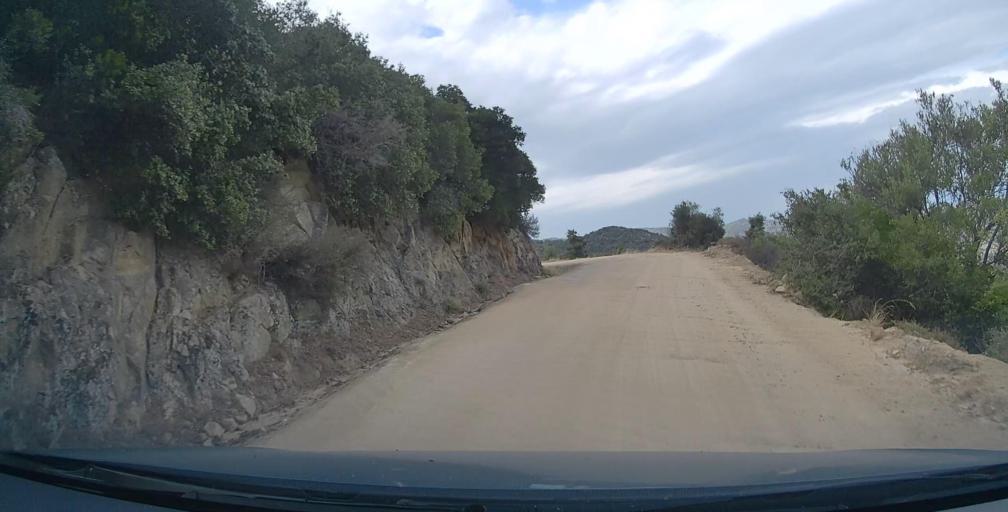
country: GR
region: Central Macedonia
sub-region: Nomos Chalkidikis
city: Sykia
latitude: 40.0148
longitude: 23.9365
